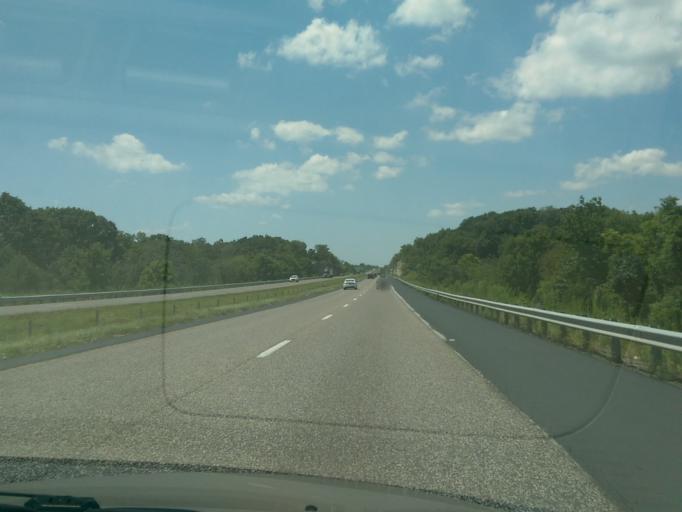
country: US
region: Missouri
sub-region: Cooper County
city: Boonville
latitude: 38.9394
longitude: -92.6130
